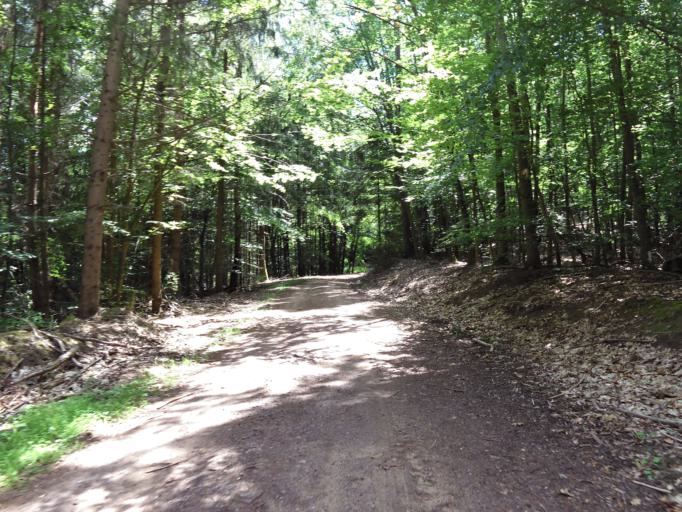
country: DE
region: Rheinland-Pfalz
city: Altleiningen
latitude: 49.4686
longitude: 8.0653
